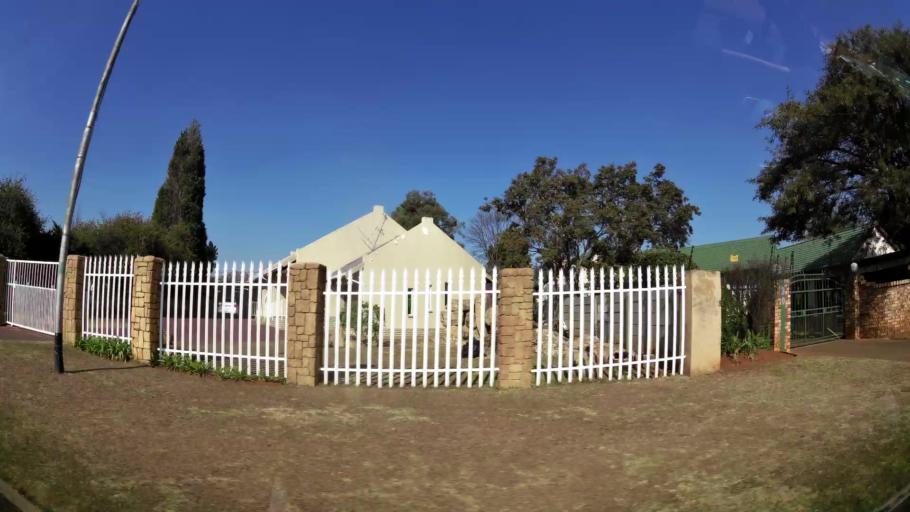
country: ZA
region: Gauteng
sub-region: West Rand District Municipality
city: Randfontein
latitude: -26.1608
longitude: 27.6927
